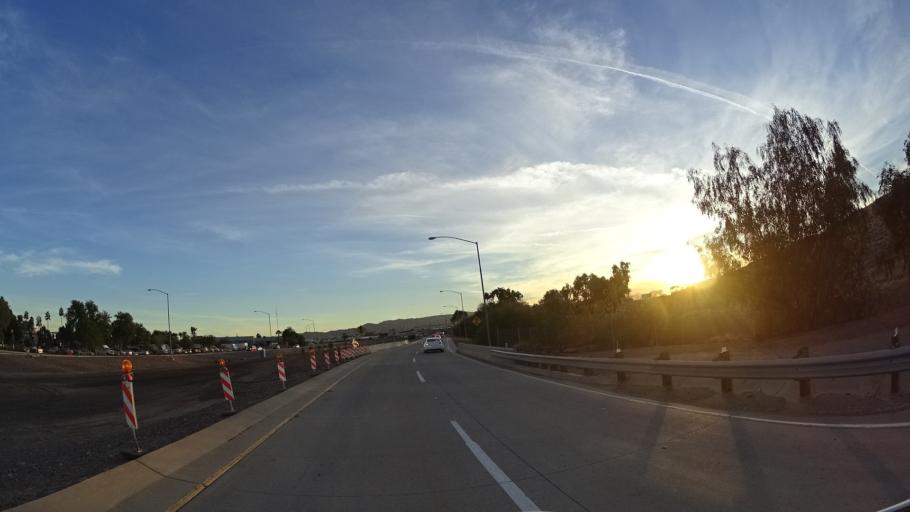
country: US
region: Arizona
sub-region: Maricopa County
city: Tempe Junction
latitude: 33.4251
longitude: -111.9843
